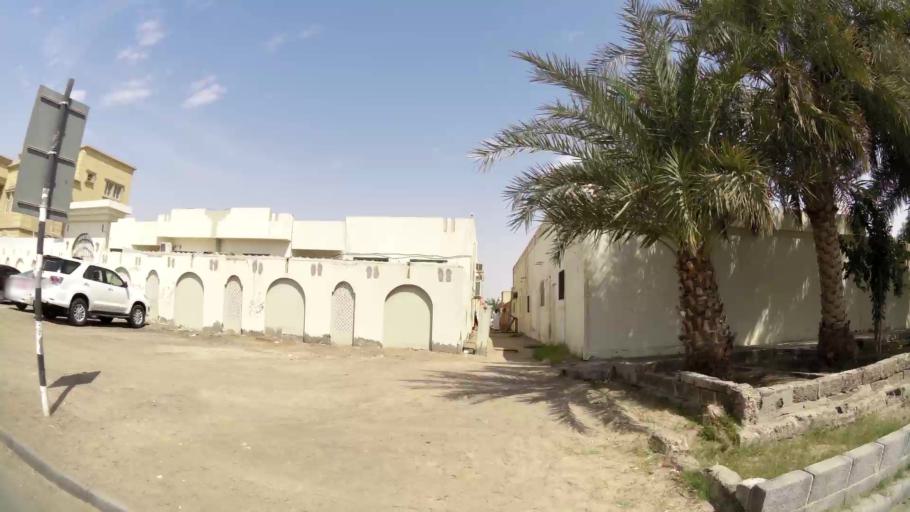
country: AE
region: Abu Dhabi
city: Abu Dhabi
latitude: 24.2894
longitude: 54.6521
